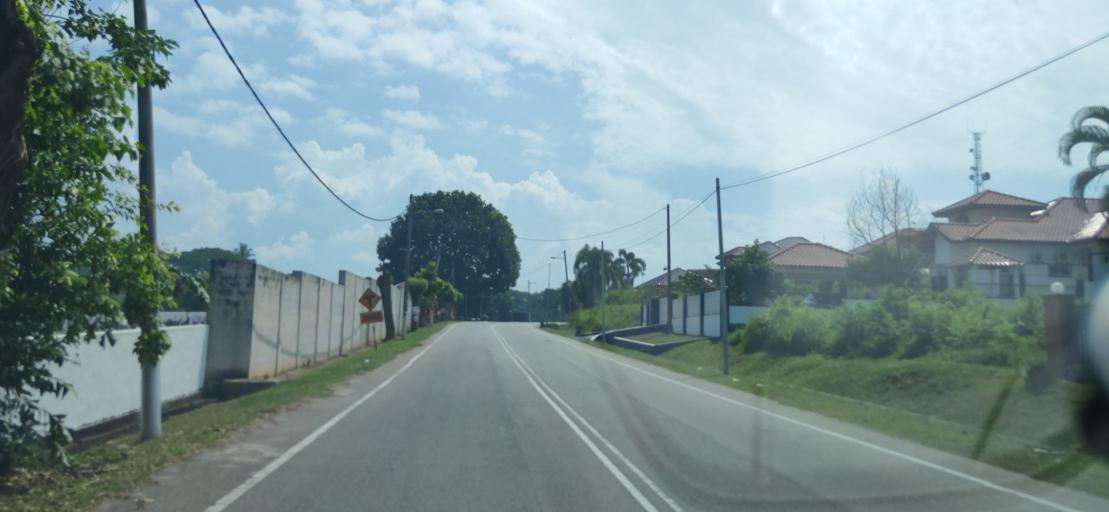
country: MY
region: Kedah
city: Sungai Petani
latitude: 5.6491
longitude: 100.4811
